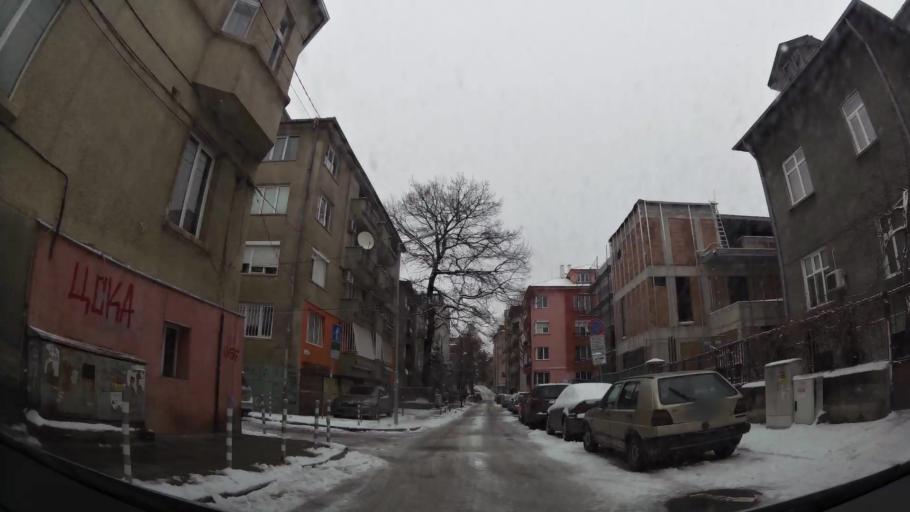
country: BG
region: Sofia-Capital
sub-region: Stolichna Obshtina
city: Sofia
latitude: 42.6883
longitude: 23.3435
